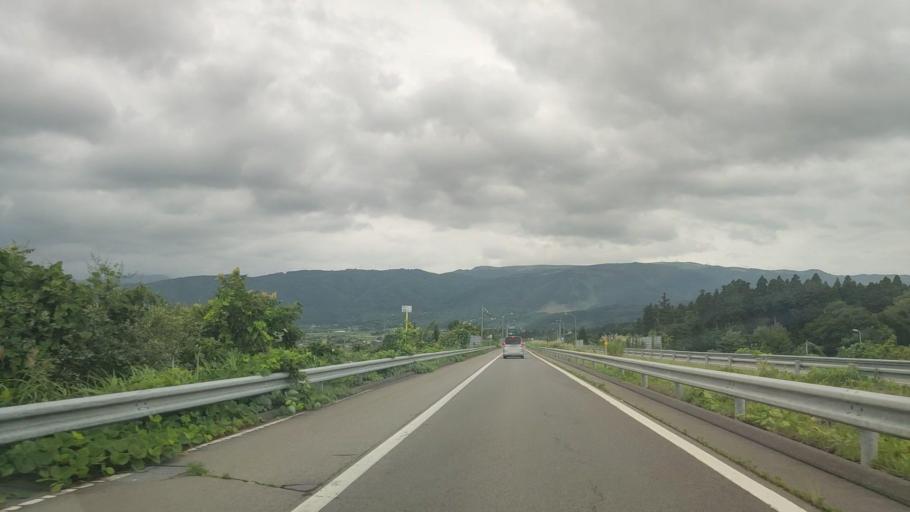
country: JP
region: Hokkaido
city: Nanae
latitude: 41.9210
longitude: 140.6772
